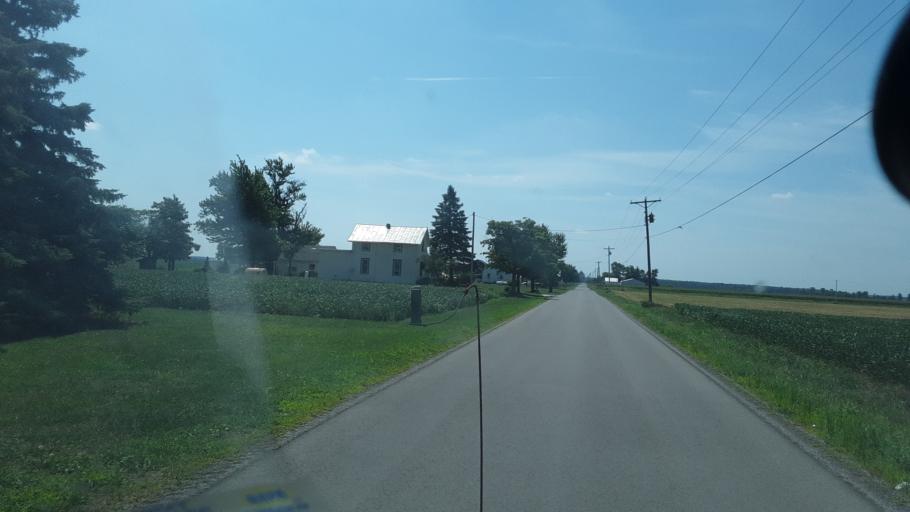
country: US
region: Ohio
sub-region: Hancock County
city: Findlay
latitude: 41.0100
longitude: -83.5159
